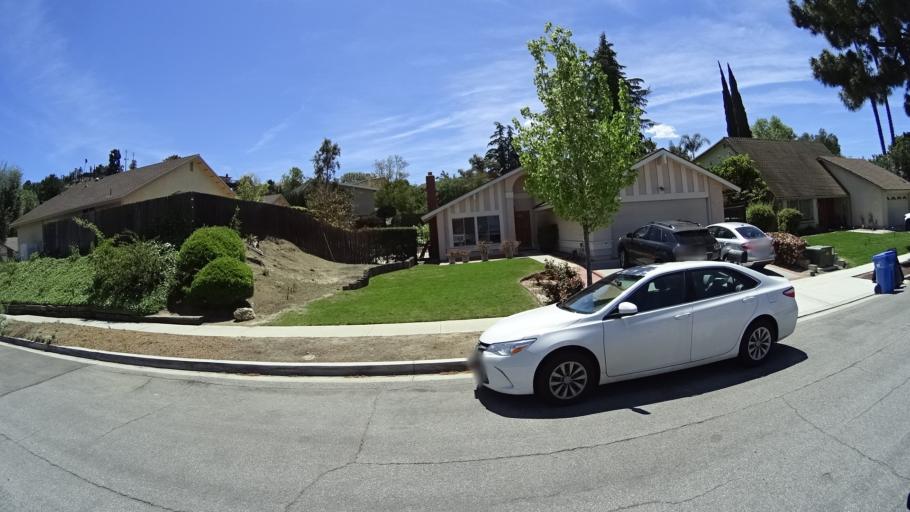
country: US
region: California
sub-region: Ventura County
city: Moorpark
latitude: 34.2308
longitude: -118.8540
